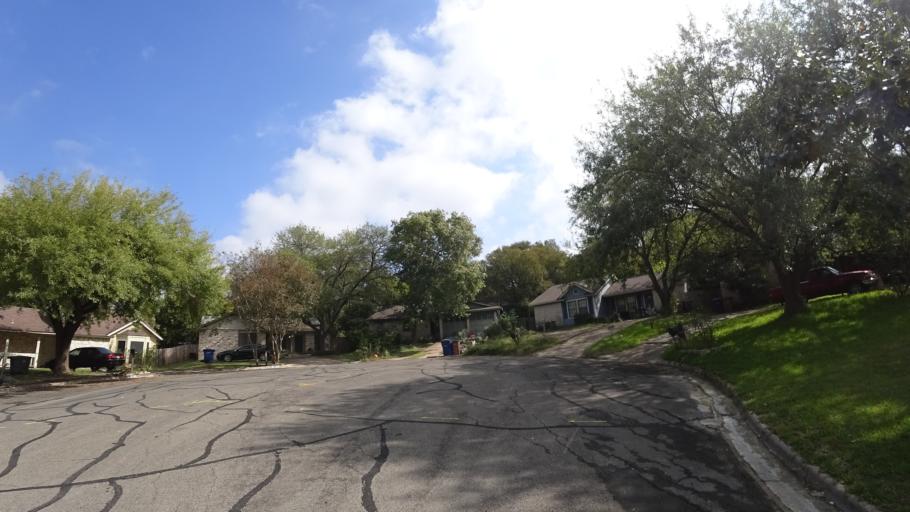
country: US
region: Texas
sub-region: Travis County
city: Shady Hollow
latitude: 30.2011
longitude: -97.8312
